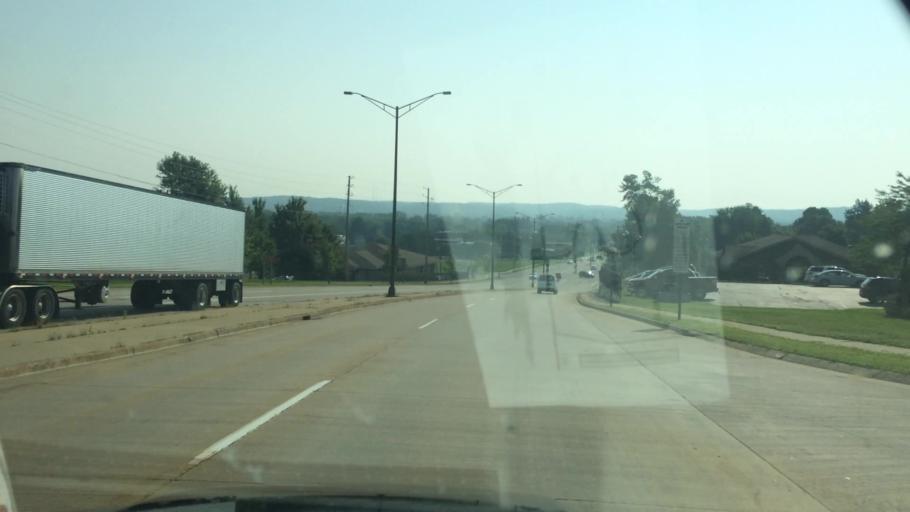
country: US
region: Wisconsin
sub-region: Marathon County
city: Wausau
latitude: 44.9698
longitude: -89.6552
